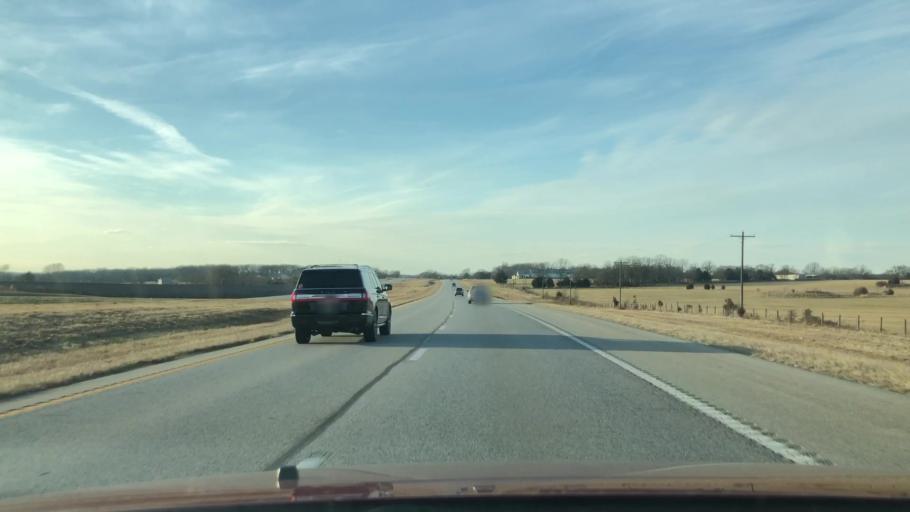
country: US
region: Missouri
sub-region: Webster County
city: Seymour
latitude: 37.1244
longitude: -92.7026
